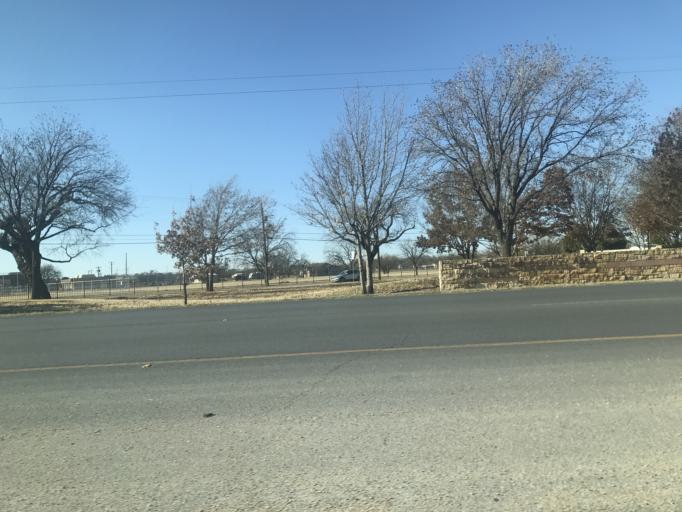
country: US
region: Texas
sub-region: Taylor County
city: Abilene
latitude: 32.4174
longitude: -99.7419
